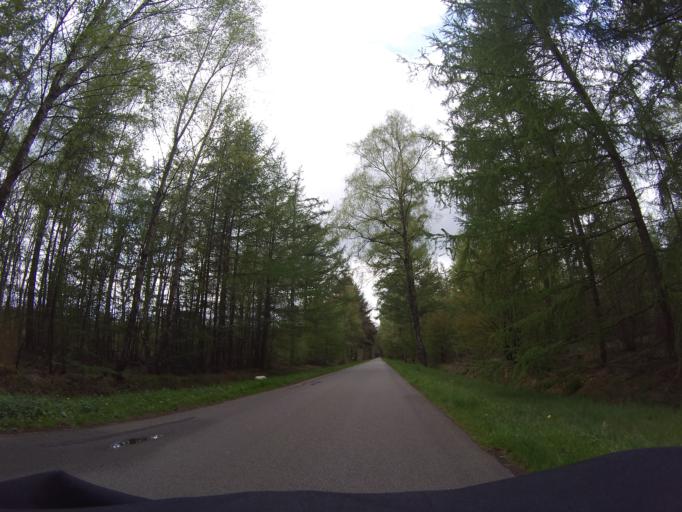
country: NL
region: Overijssel
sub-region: Gemeente Twenterand
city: Den Ham
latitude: 52.5119
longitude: 6.4691
